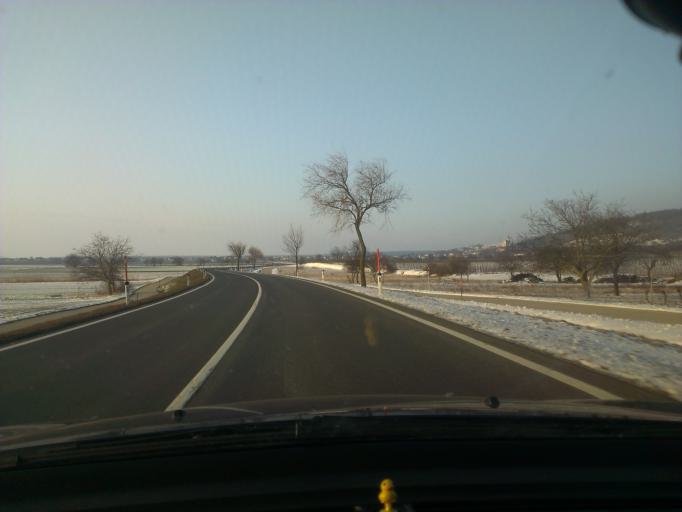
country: AT
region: Burgenland
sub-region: Eisenstadt-Umgebung
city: Donnerskirchen
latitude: 47.9054
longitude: 16.6596
